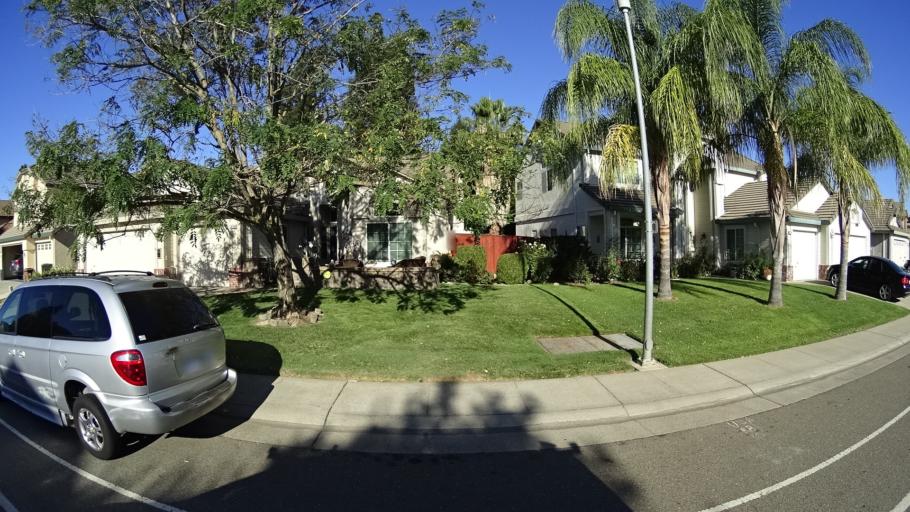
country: US
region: California
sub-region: Sacramento County
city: Elk Grove
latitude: 38.4402
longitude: -121.3789
